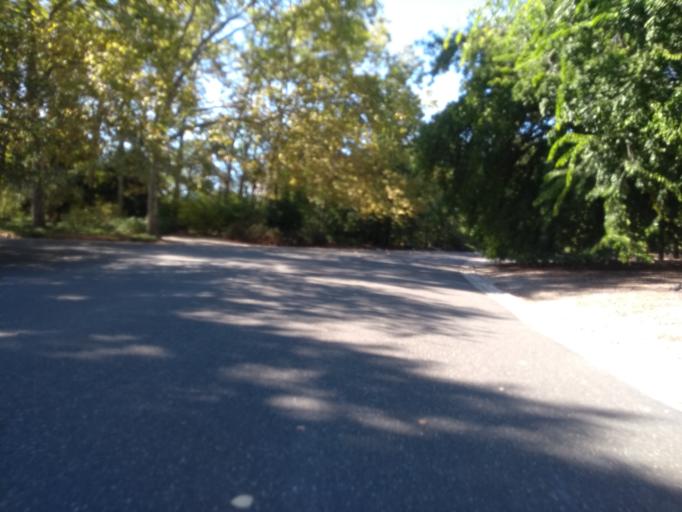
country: FR
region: Aquitaine
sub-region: Departement de la Gironde
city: Le Bouscat
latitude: 44.8511
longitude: -0.6025
